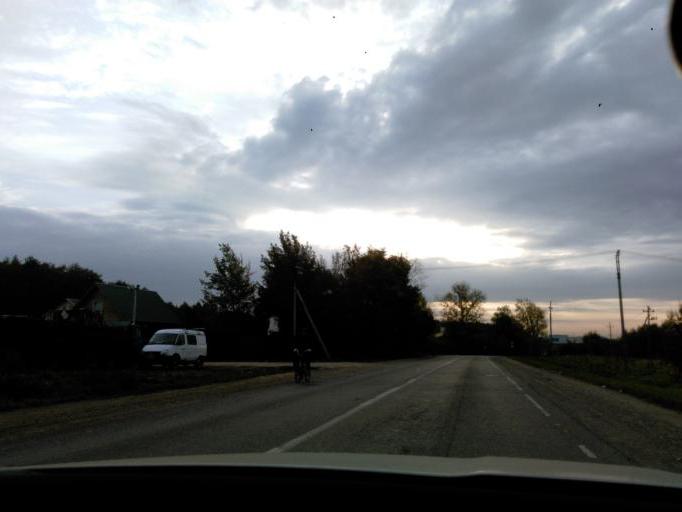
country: RU
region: Moskovskaya
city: Sheremet'yevskiy
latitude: 55.9727
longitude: 37.4641
